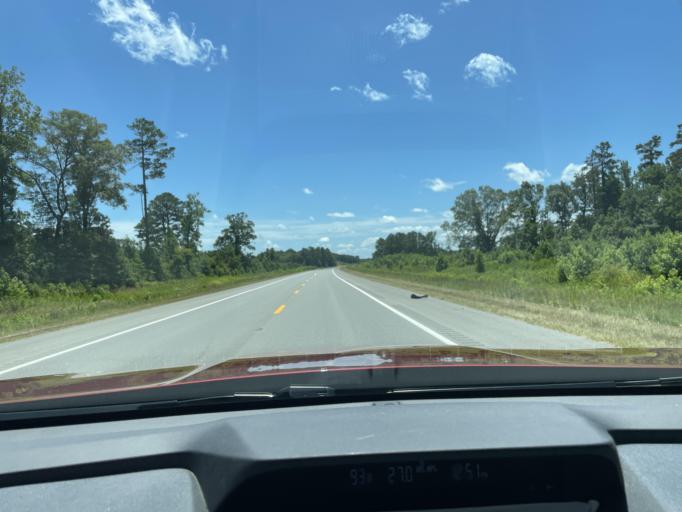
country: US
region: Arkansas
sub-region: Lincoln County
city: Star City
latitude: 33.9388
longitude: -91.8934
